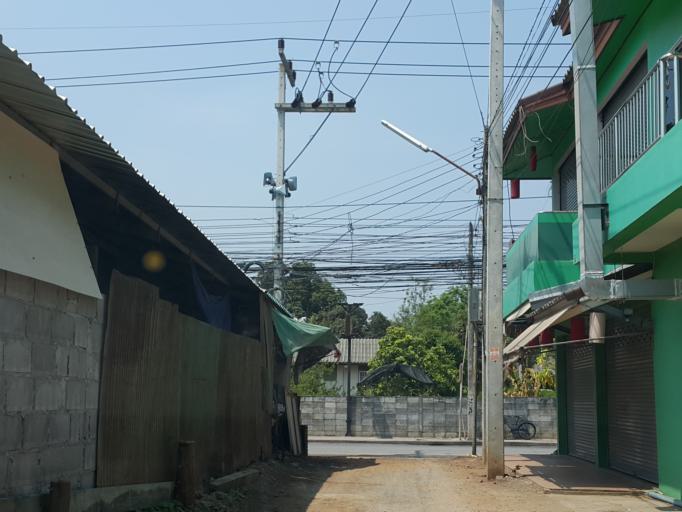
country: TH
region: Kanchanaburi
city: Kanchanaburi
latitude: 14.0347
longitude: 99.5194
